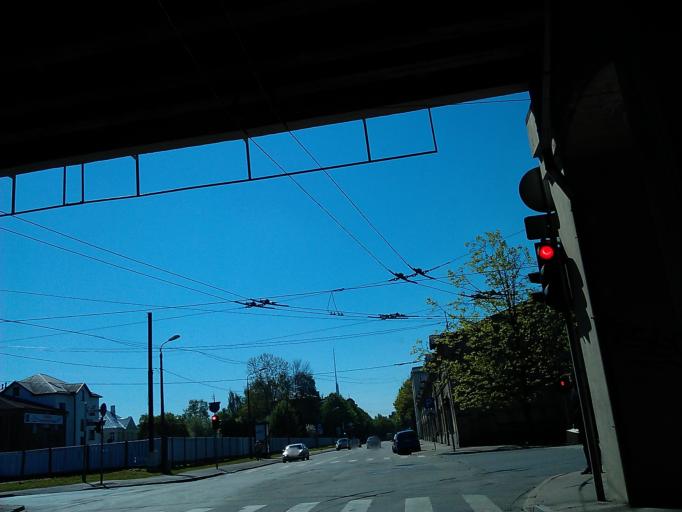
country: LV
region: Riga
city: Riga
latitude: 56.9462
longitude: 24.1258
